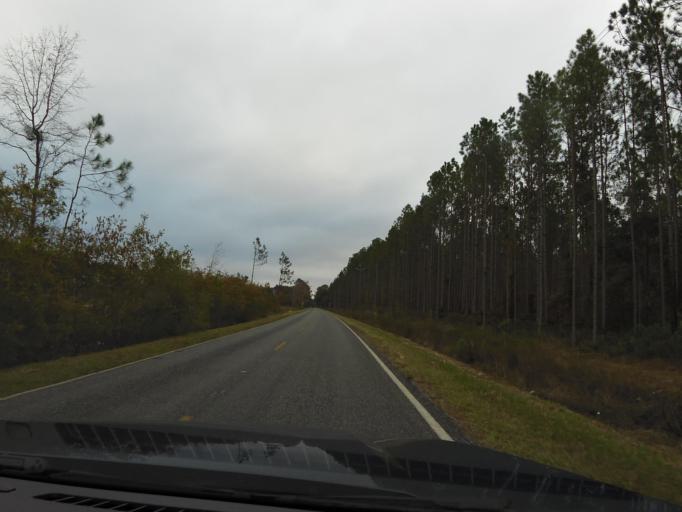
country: US
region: Georgia
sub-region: Charlton County
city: Folkston
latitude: 30.8674
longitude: -82.0404
